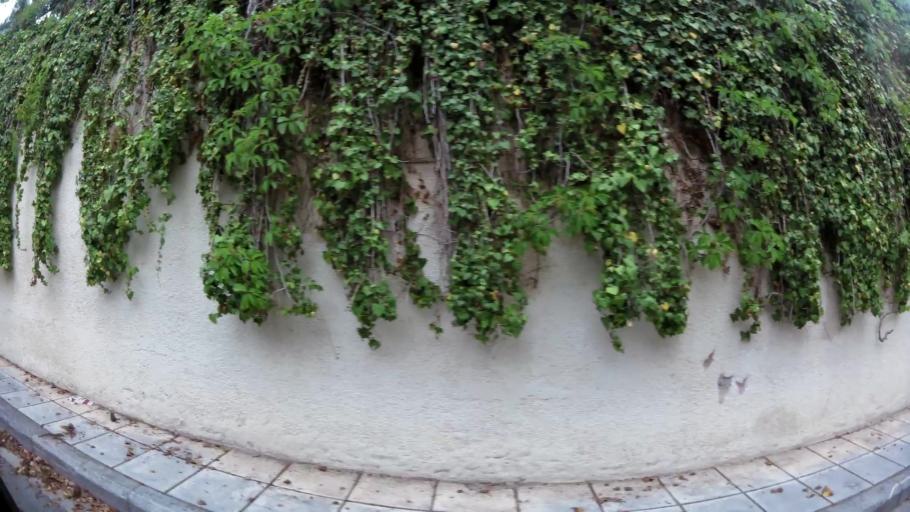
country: GR
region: Central Macedonia
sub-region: Nomos Thessalonikis
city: Panorama
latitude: 40.5871
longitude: 23.0230
